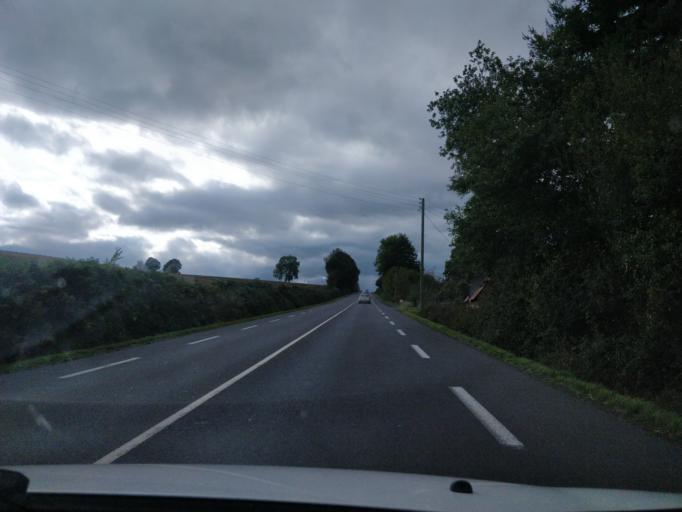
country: FR
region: Lower Normandy
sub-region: Departement du Calvados
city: Vire
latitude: 48.8439
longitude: -0.9203
